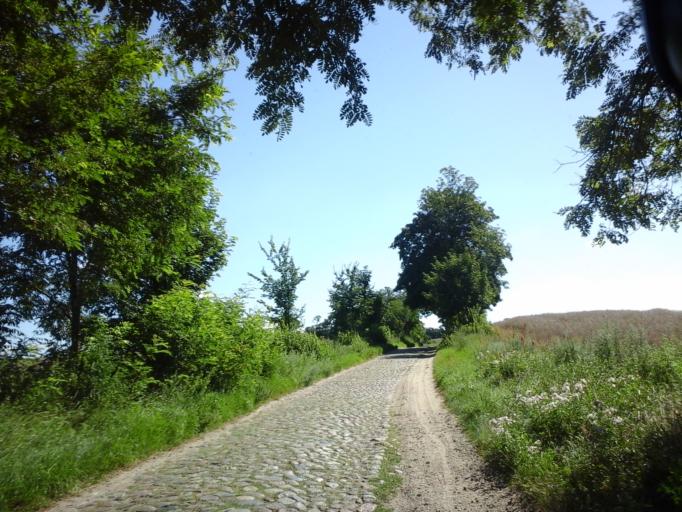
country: PL
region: West Pomeranian Voivodeship
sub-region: Powiat choszczenski
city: Choszczno
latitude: 53.1870
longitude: 15.4665
